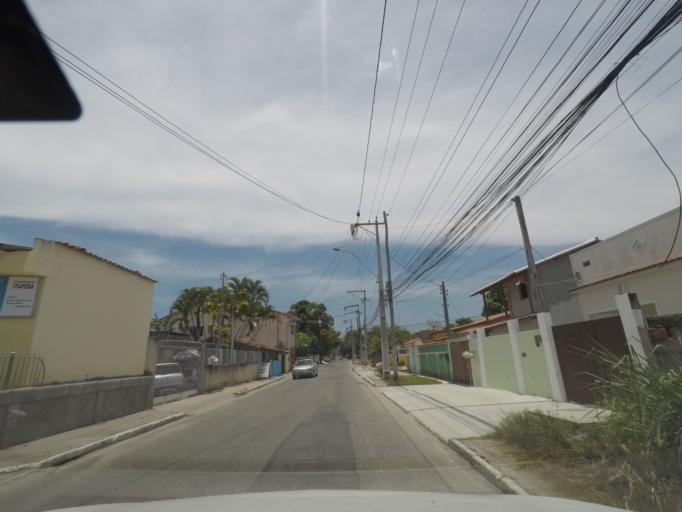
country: BR
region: Rio de Janeiro
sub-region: Marica
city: Marica
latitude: -22.9100
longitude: -42.8383
